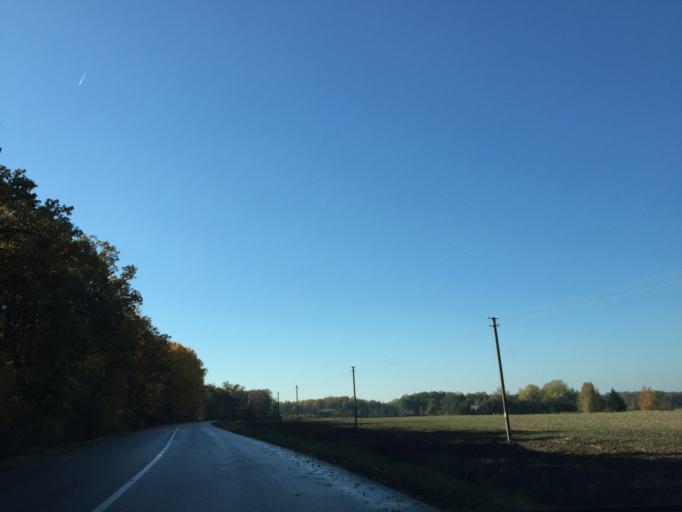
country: LT
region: Klaipedos apskritis
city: Kretinga
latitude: 55.8732
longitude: 21.3224
